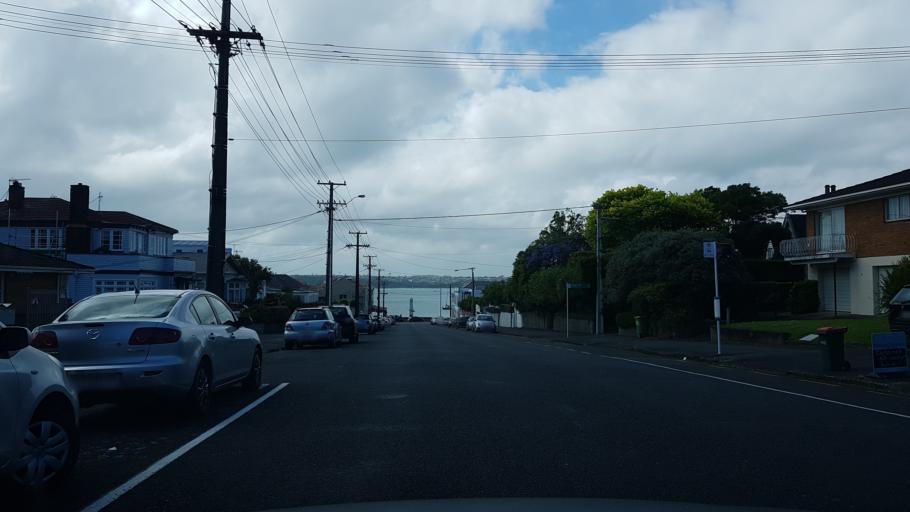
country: NZ
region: Auckland
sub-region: Auckland
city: Auckland
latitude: -36.8284
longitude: 174.8028
